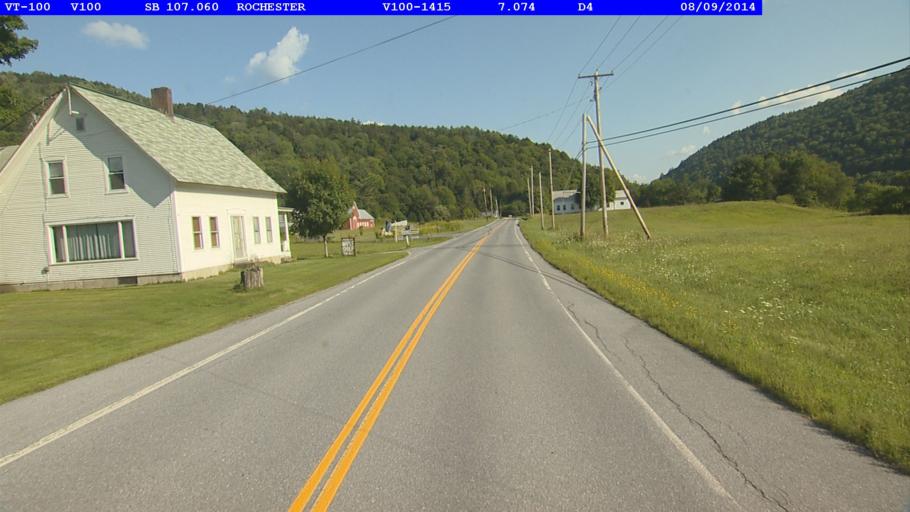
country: US
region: Vermont
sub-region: Orange County
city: Randolph
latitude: 43.8967
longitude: -72.8202
